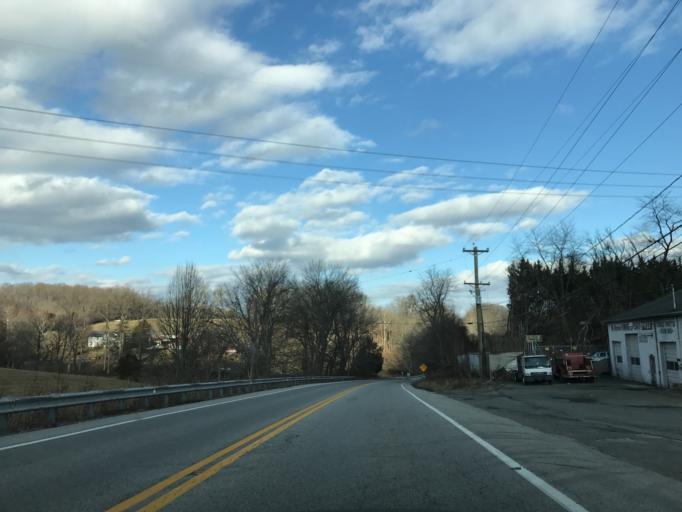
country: US
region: Maryland
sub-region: Cecil County
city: Rising Sun
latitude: 39.6879
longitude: -76.1355
